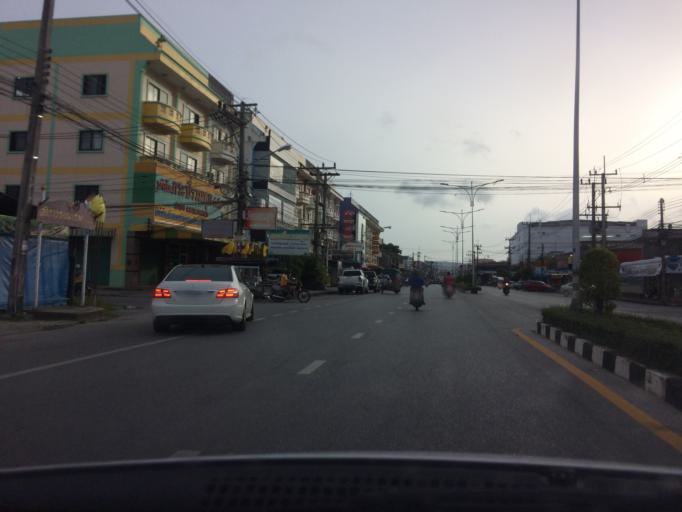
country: TH
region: Phuket
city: Ban Talat Yai
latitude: 7.8783
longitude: 98.3972
